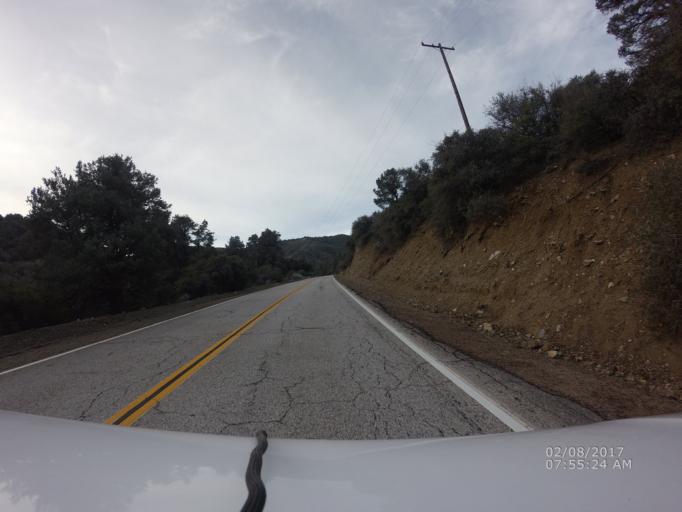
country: US
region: California
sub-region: San Bernardino County
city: Pinon Hills
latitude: 34.4168
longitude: -117.7683
